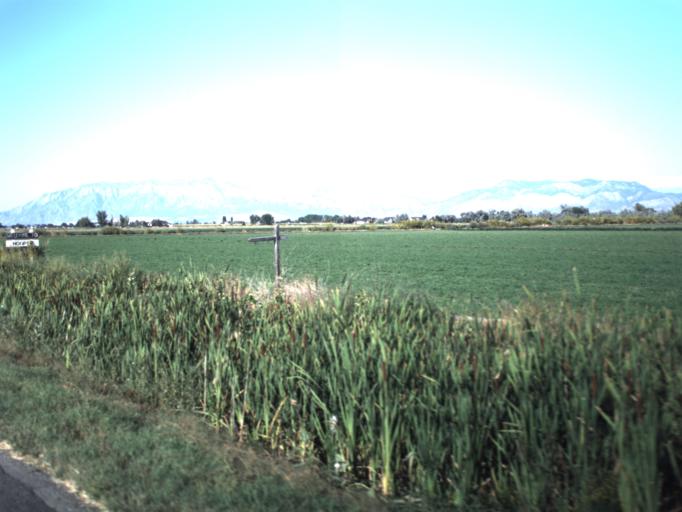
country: US
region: Utah
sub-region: Weber County
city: Hooper
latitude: 41.1416
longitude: -112.1229
